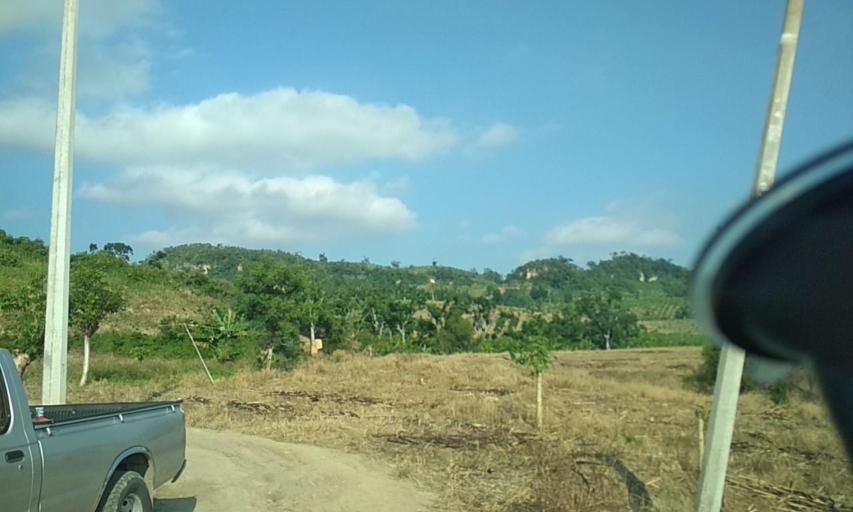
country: MX
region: Veracruz
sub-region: Papantla
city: Polutla
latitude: 20.6004
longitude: -97.2575
